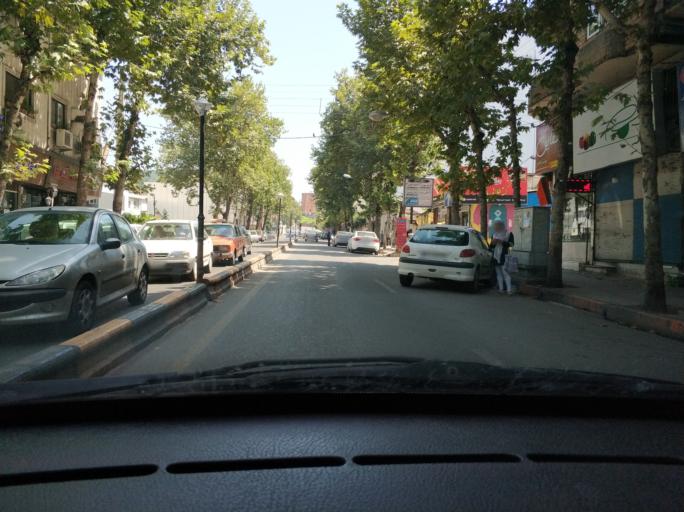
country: IR
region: Gilan
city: Lahijan
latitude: 37.1981
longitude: 50.0119
